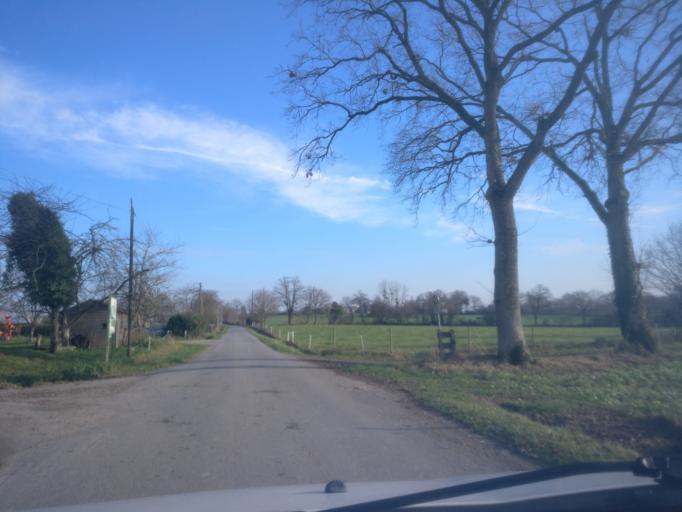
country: FR
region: Brittany
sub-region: Departement d'Ille-et-Vilaine
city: Livre-sur-Changeon
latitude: 48.2048
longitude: -1.2880
